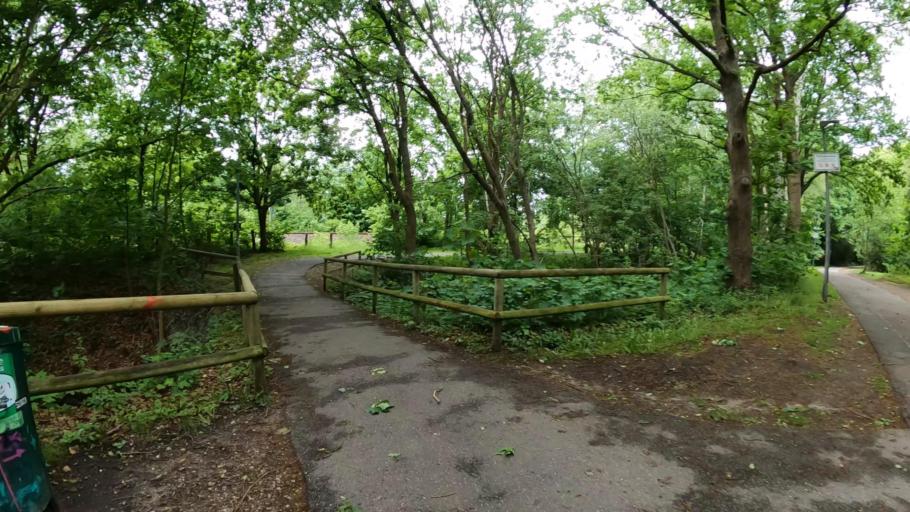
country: DE
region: Schleswig-Holstein
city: Norderstedt
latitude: 53.7140
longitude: 9.9924
